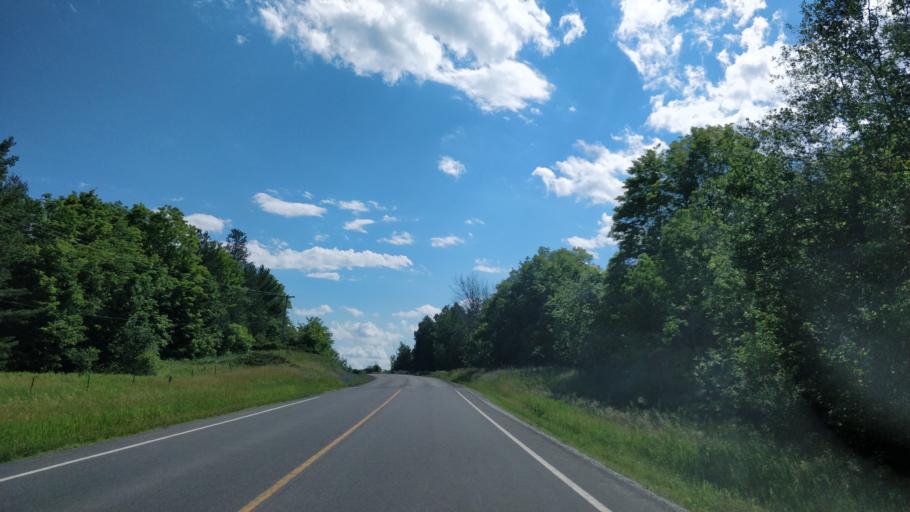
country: CA
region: Ontario
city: Perth
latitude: 44.7771
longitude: -76.4506
